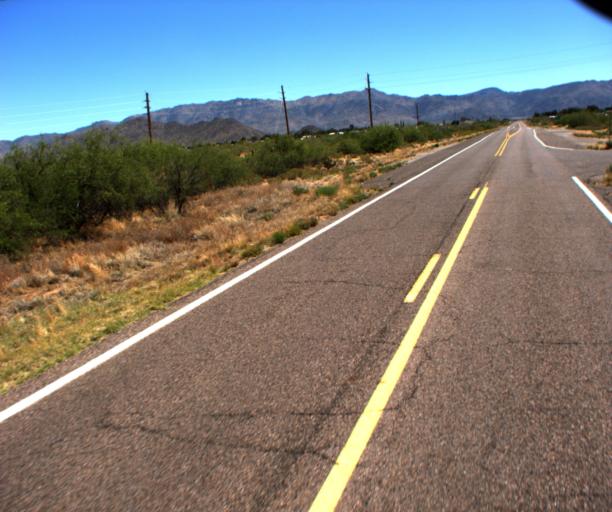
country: US
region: Arizona
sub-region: Yavapai County
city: Congress
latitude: 34.1575
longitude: -112.8645
